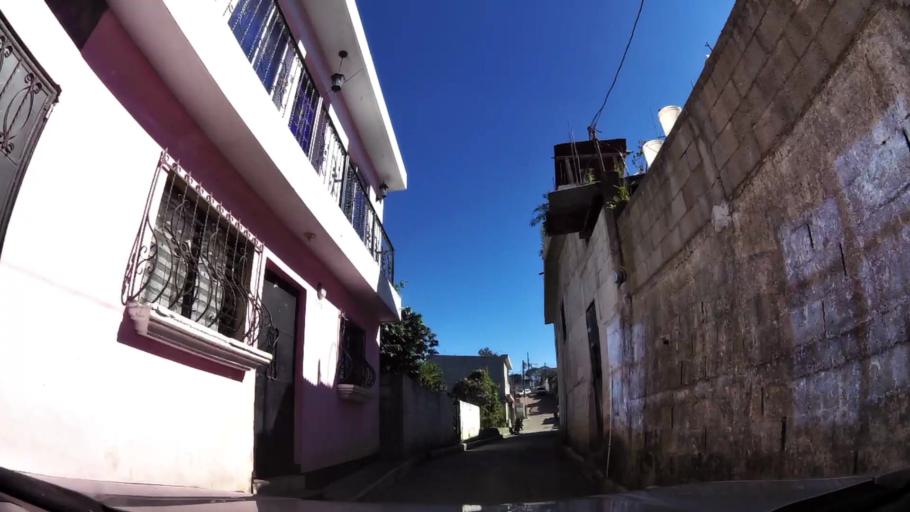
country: GT
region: Guatemala
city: Fraijanes
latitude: 14.4584
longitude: -90.4398
